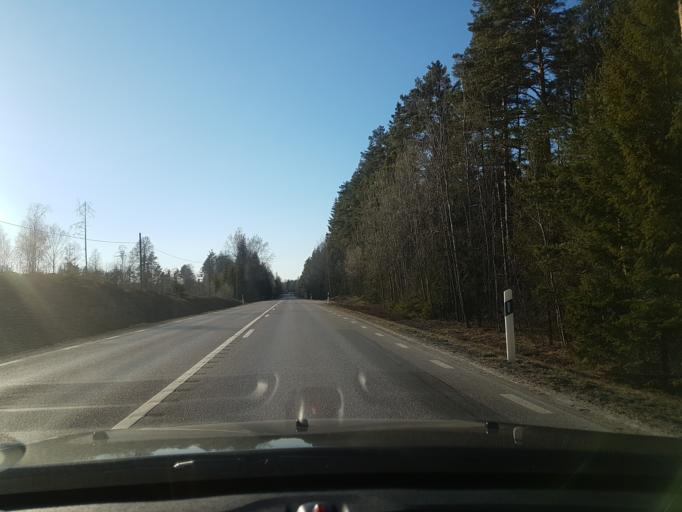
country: SE
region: Uppsala
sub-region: Heby Kommun
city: Morgongava
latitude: 59.8996
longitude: 17.0881
